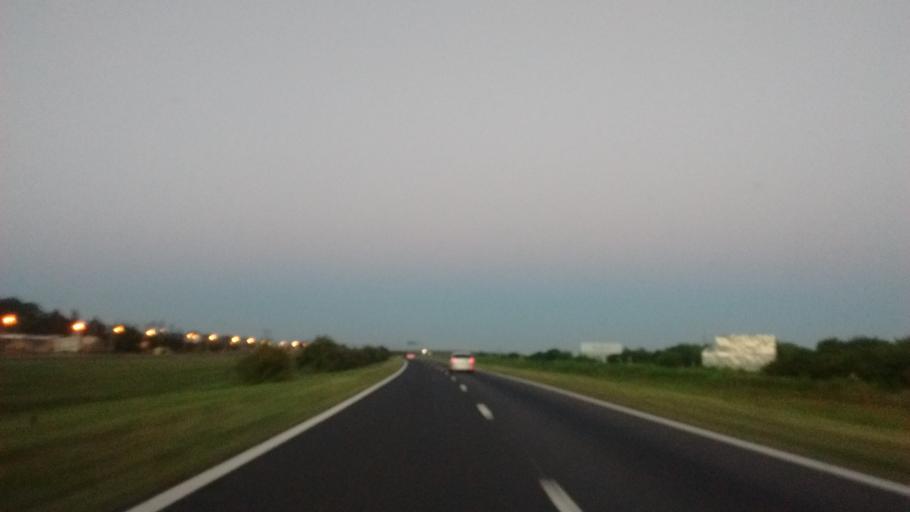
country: AR
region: Santa Fe
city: Roldan
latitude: -32.9278
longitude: -60.8877
